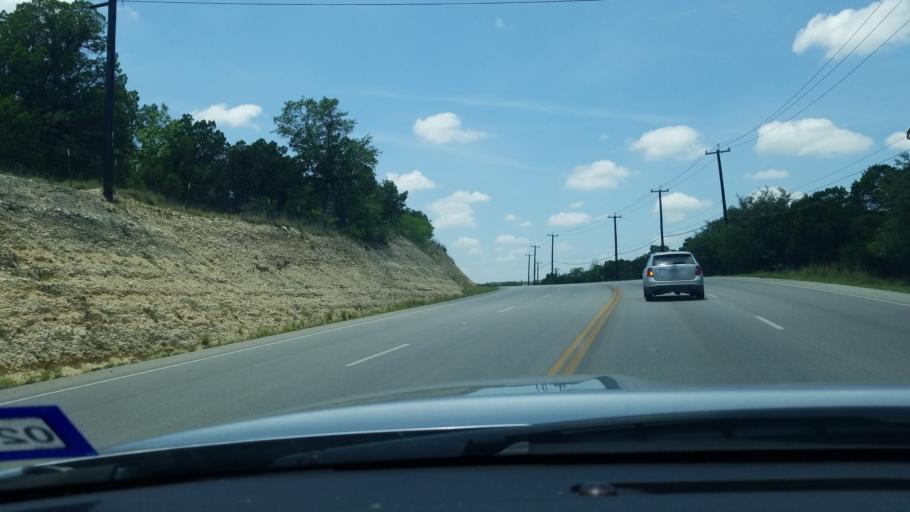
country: US
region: Texas
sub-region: Bexar County
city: Timberwood Park
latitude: 29.7135
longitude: -98.4629
